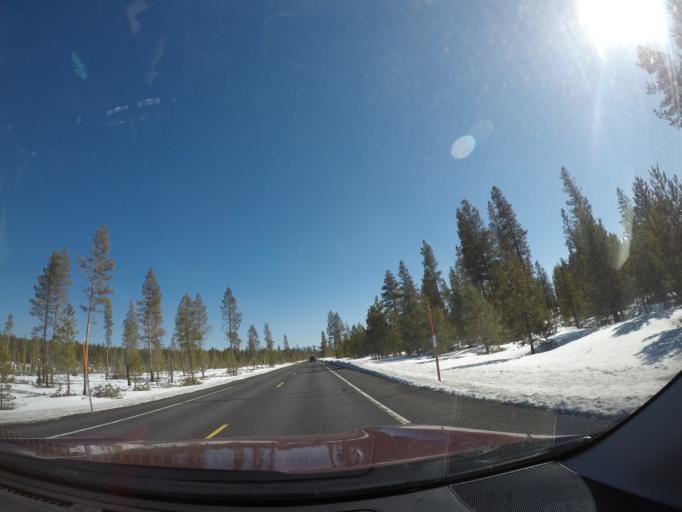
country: US
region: Oregon
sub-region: Deschutes County
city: Three Rivers
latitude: 43.8641
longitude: -121.5361
